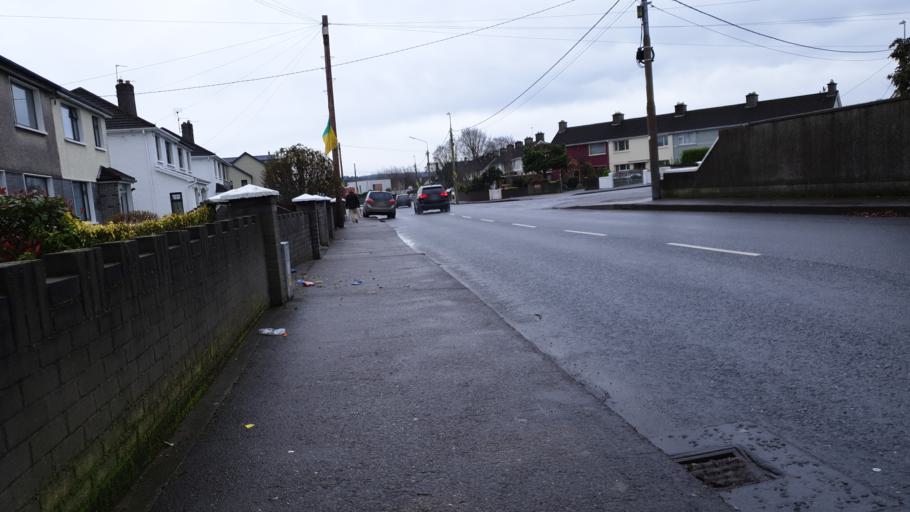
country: IE
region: Munster
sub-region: County Cork
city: Cork
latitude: 51.8920
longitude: -8.4195
